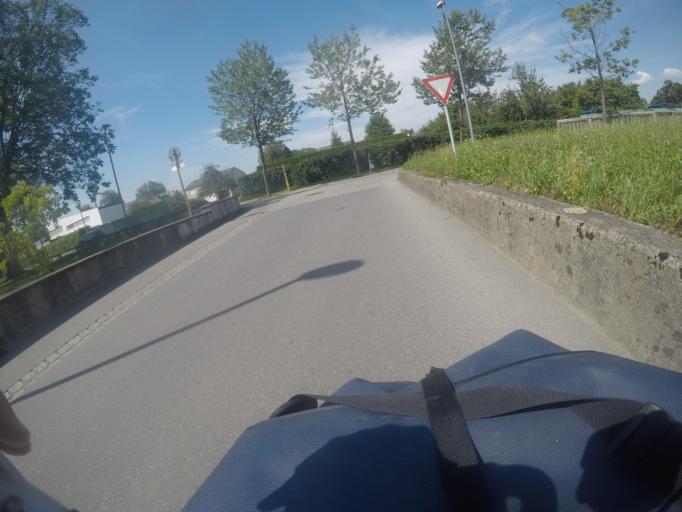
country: AT
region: Vorarlberg
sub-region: Politischer Bezirk Dornbirn
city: Lustenau
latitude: 47.4353
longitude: 9.6742
